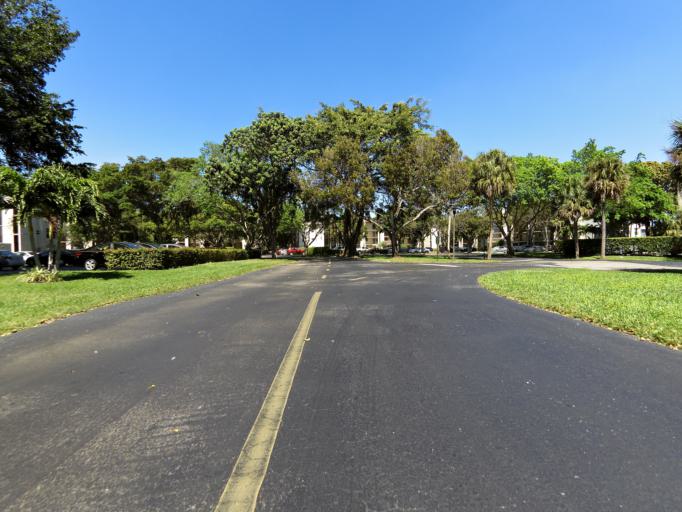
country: US
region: Florida
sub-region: Broward County
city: Pine Island Ridge
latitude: 26.0980
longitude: -80.2737
